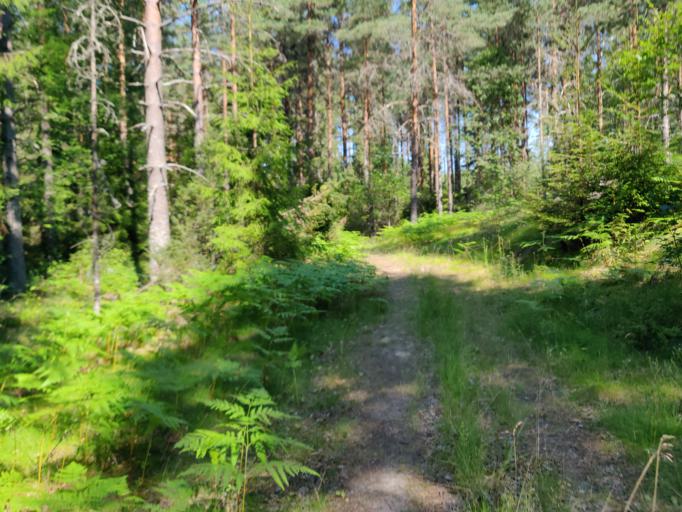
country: SE
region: Vaermland
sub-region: Hagfors Kommun
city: Hagfors
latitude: 60.0162
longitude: 13.5661
